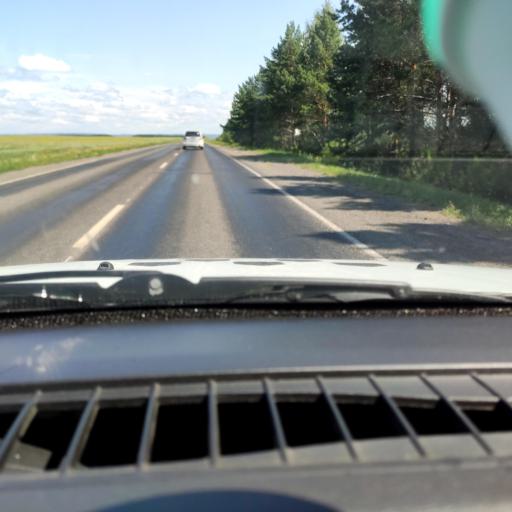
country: RU
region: Bashkortostan
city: Verkhniye Kigi
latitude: 55.4597
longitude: 58.4540
